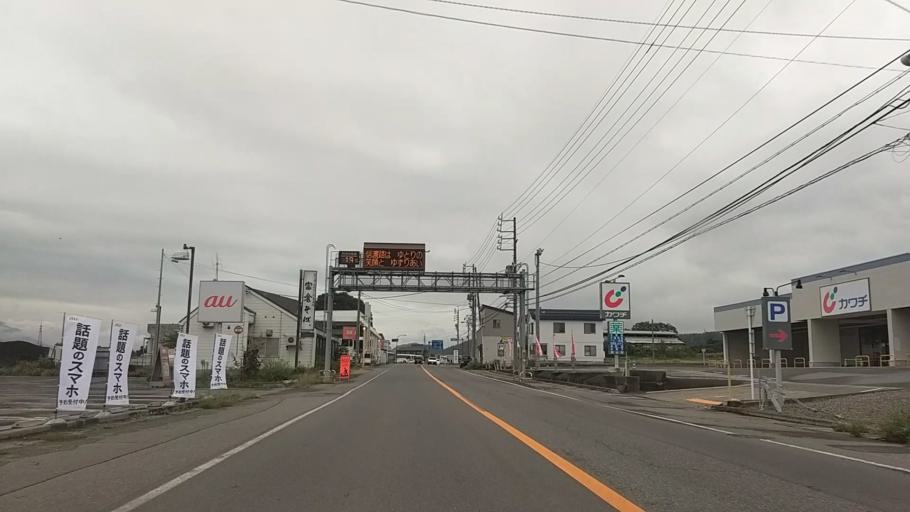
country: JP
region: Nagano
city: Iiyama
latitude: 36.8290
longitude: 138.3544
